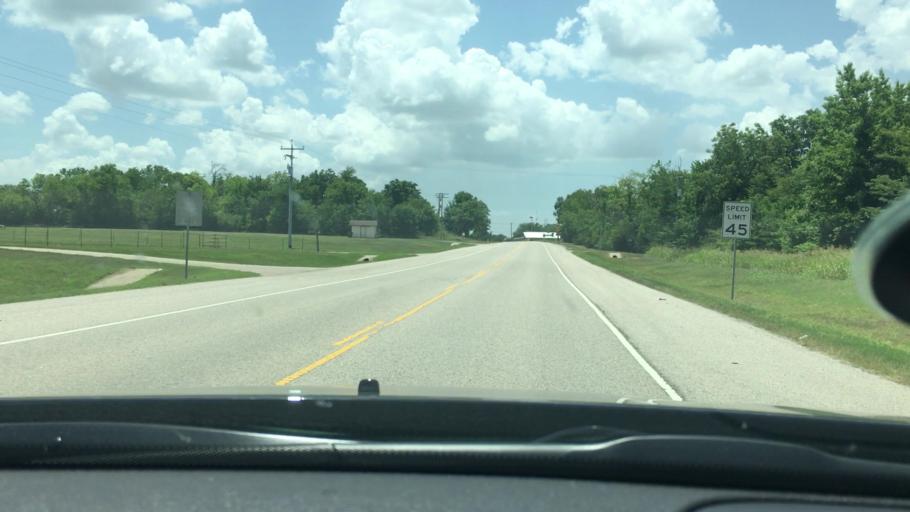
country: US
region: Oklahoma
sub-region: Johnston County
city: Tishomingo
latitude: 34.4521
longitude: -96.6359
